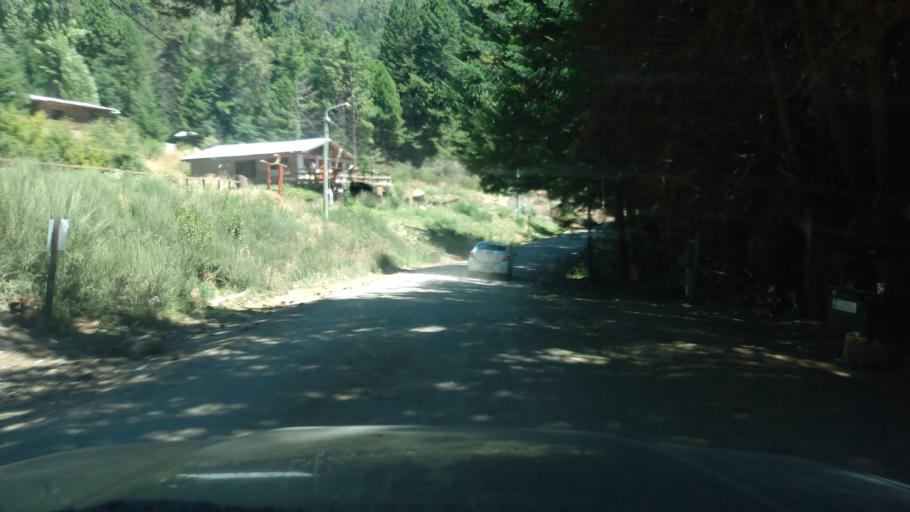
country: AR
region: Rio Negro
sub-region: Departamento de Bariloche
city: San Carlos de Bariloche
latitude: -41.1013
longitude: -71.4954
